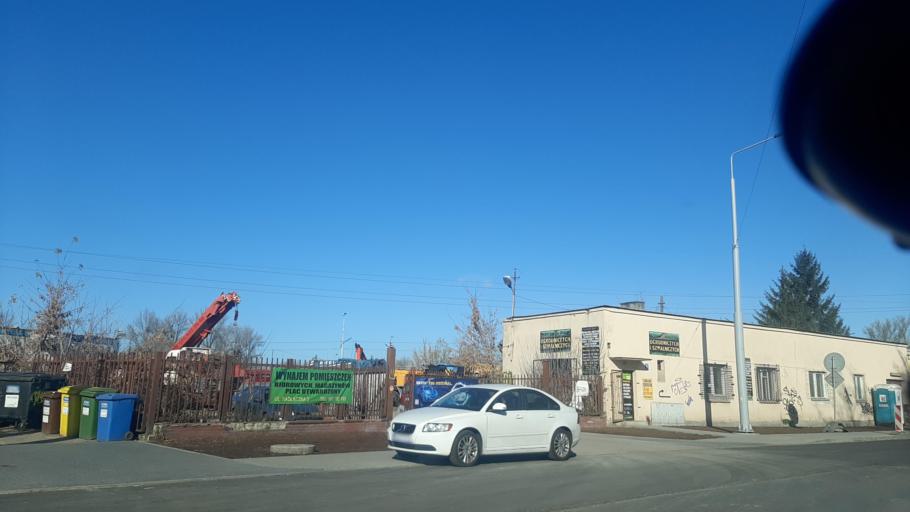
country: PL
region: Lublin Voivodeship
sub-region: Powiat lubelski
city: Lublin
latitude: 51.2321
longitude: 22.5659
